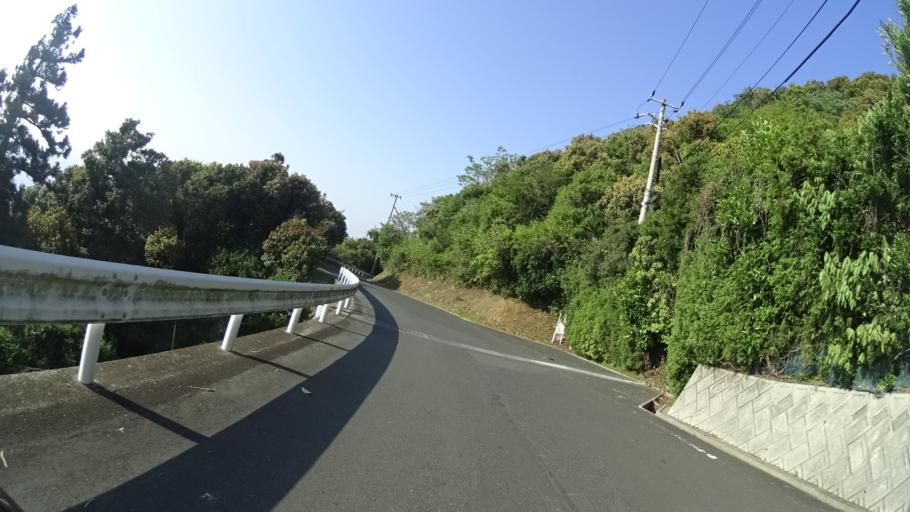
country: JP
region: Ehime
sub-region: Nishiuwa-gun
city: Ikata-cho
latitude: 33.3712
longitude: 132.0573
